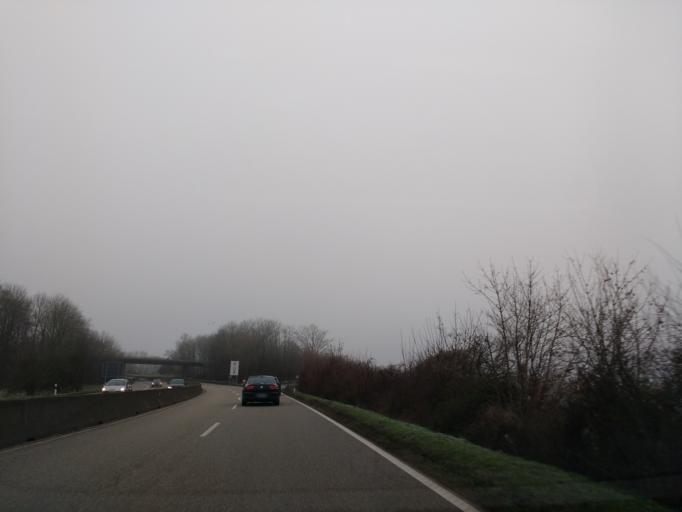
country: DE
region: Baden-Wuerttemberg
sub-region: Freiburg Region
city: Kehl
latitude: 48.5760
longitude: 7.8299
